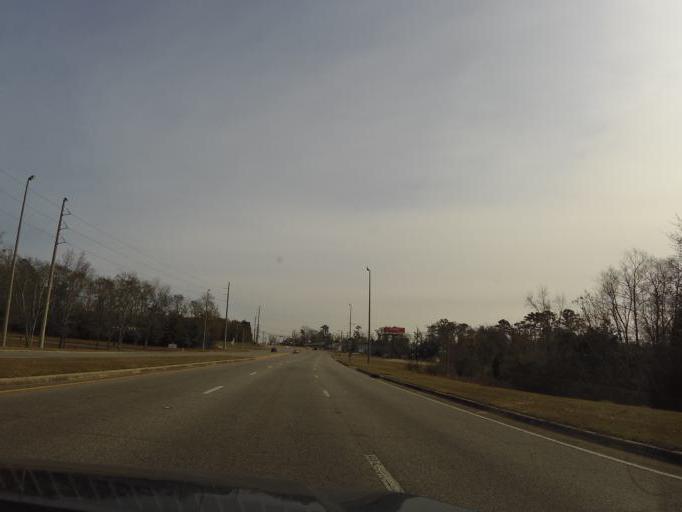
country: US
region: Alabama
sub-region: Houston County
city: Dothan
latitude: 31.2217
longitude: -85.3720
